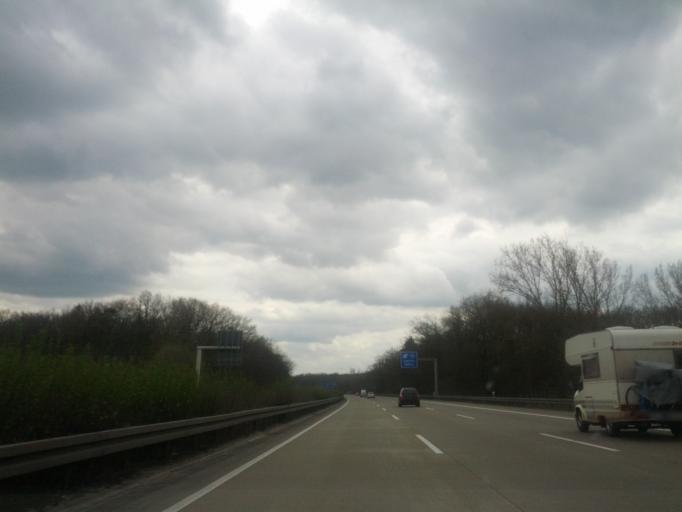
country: DE
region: Lower Saxony
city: Laatzen
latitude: 52.3245
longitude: 9.8636
